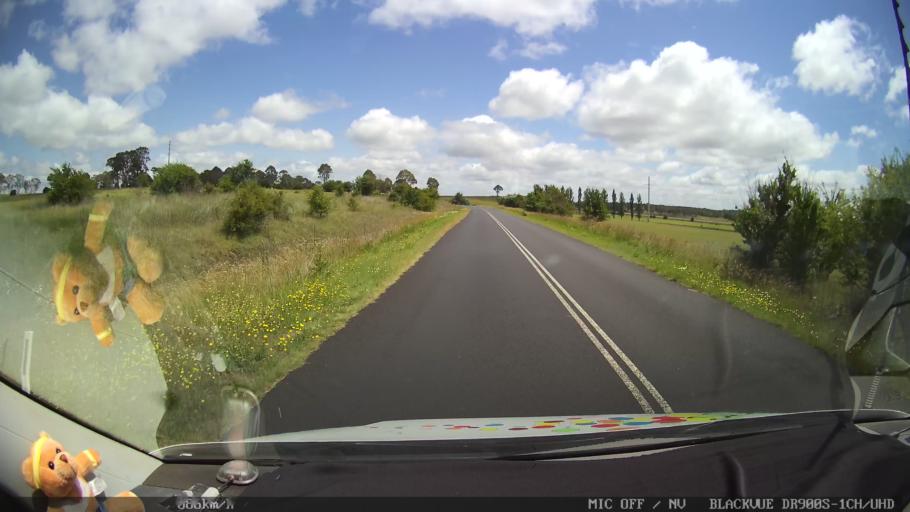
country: AU
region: New South Wales
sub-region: Glen Innes Severn
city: Glen Innes
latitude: -29.7017
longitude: 151.7189
